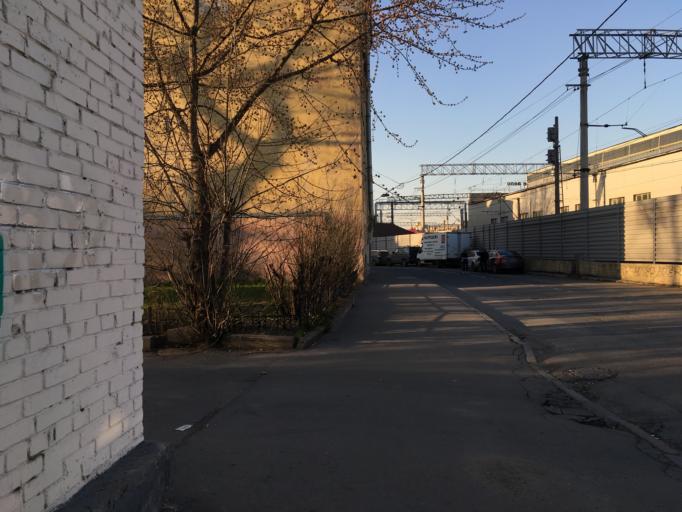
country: RU
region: St.-Petersburg
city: Centralniy
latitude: 59.9192
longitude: 30.3633
